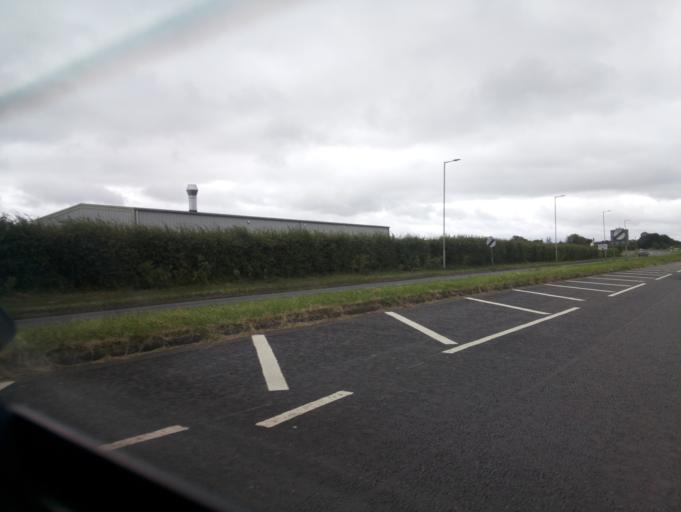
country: GB
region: England
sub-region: Gloucestershire
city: Tewkesbury
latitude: 51.9562
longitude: -2.1580
